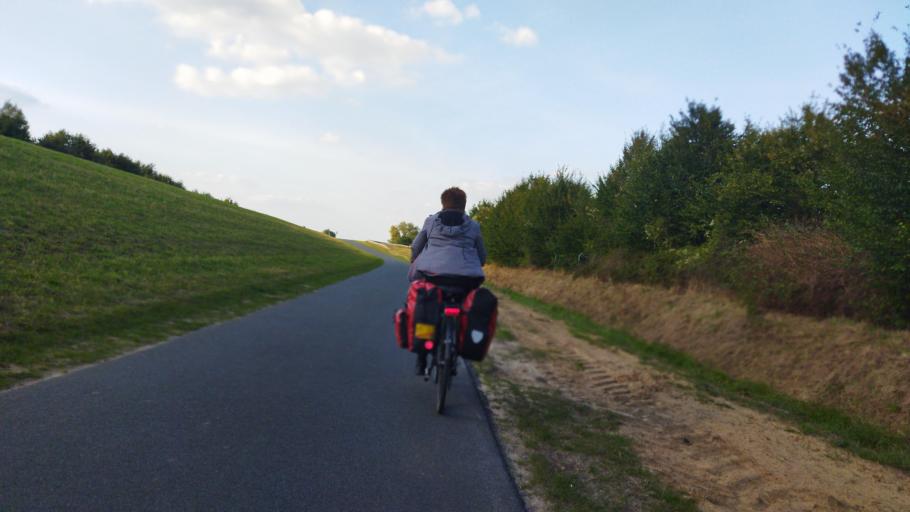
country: DE
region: Lower Saxony
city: Lehe
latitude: 53.0453
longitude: 7.3196
